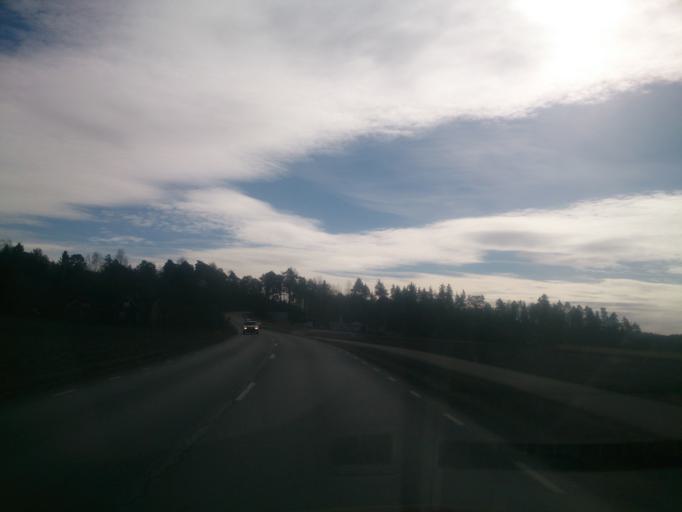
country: SE
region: OEstergoetland
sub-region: Norrkopings Kommun
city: Kimstad
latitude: 58.5586
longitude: 15.9497
